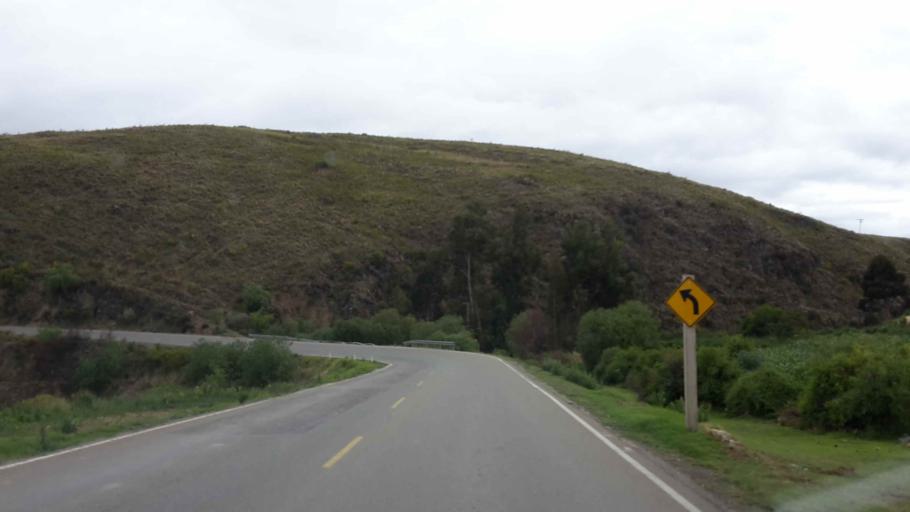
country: BO
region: Cochabamba
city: Arani
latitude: -17.4789
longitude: -65.7640
